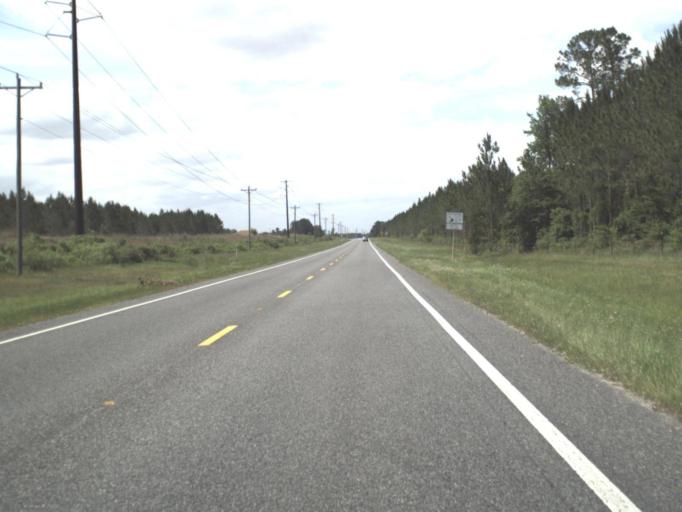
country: US
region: Florida
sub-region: Clay County
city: Middleburg
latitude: 30.0075
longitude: -81.8977
